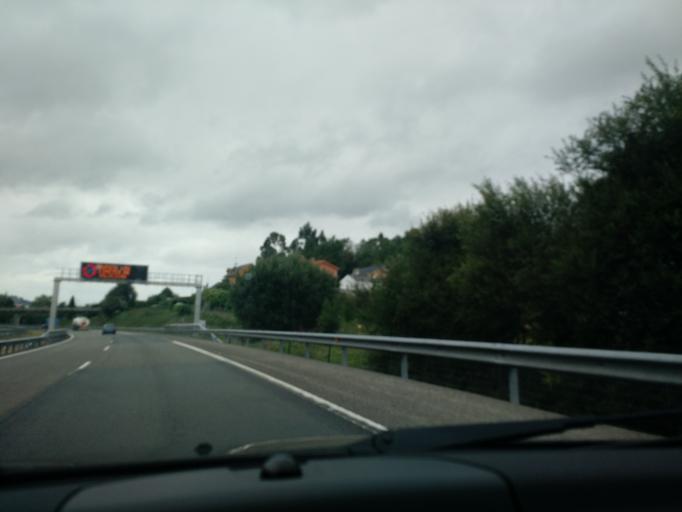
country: ES
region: Galicia
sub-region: Provincia da Coruna
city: Cambre
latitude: 43.3053
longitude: -8.3366
